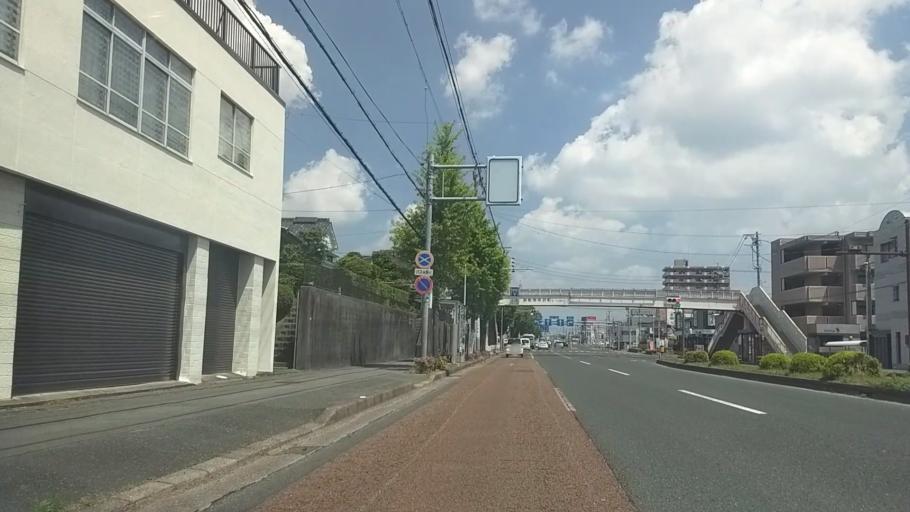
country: JP
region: Shizuoka
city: Hamamatsu
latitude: 34.7201
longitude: 137.7293
